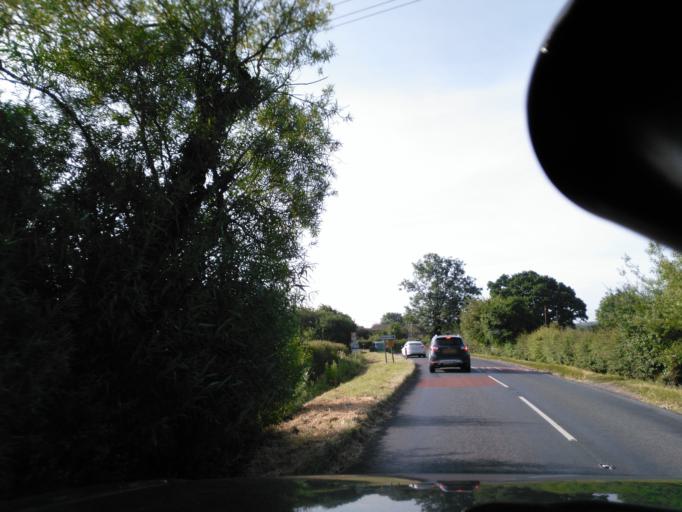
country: GB
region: England
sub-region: Wiltshire
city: Worton
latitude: 51.3181
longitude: -2.0476
